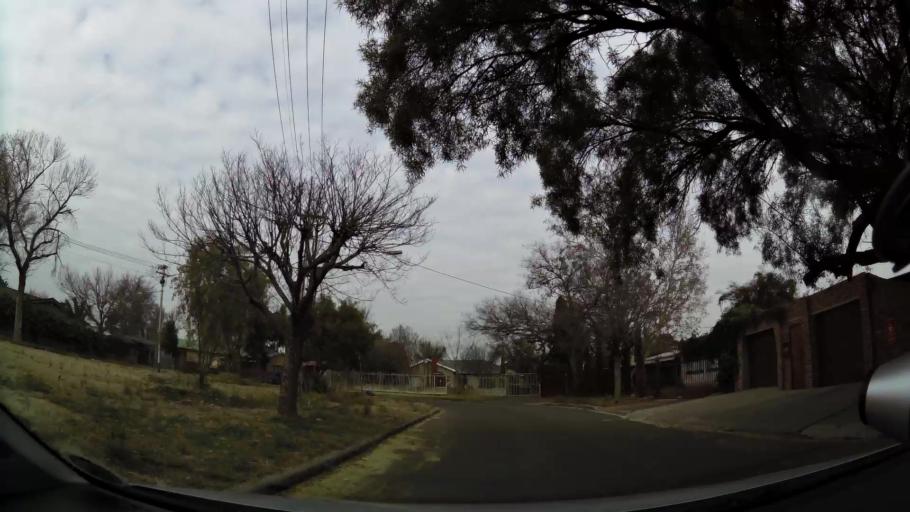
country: ZA
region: Orange Free State
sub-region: Mangaung Metropolitan Municipality
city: Bloemfontein
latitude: -29.1245
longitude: 26.1945
